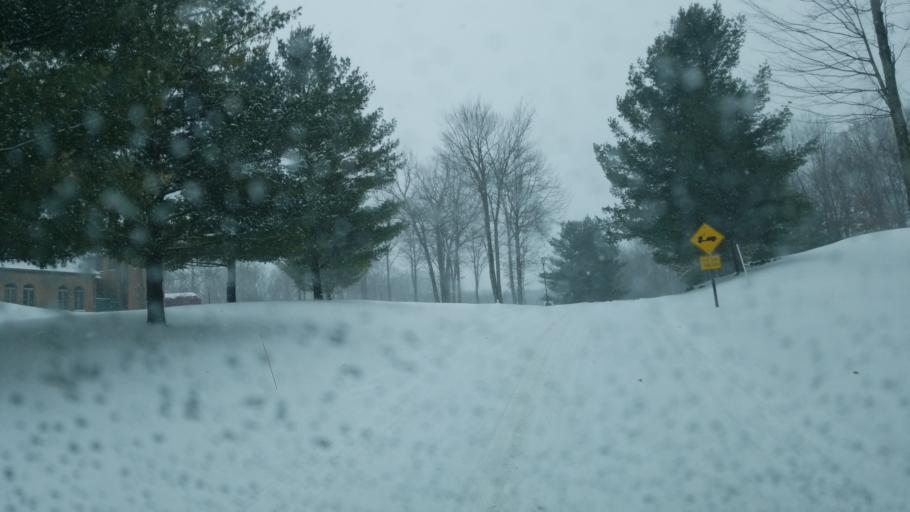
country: US
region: Michigan
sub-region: Mecosta County
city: Canadian Lakes
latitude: 43.6104
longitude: -85.3056
